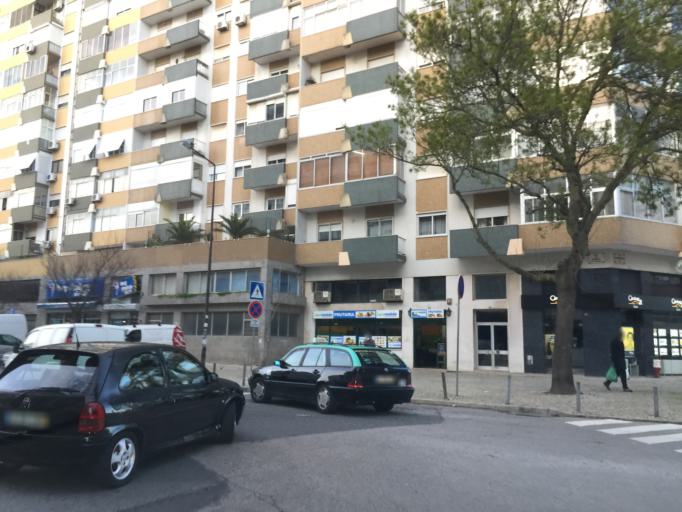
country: PT
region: Lisbon
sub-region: Odivelas
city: Olival do Basto
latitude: 38.7728
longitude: -9.1603
